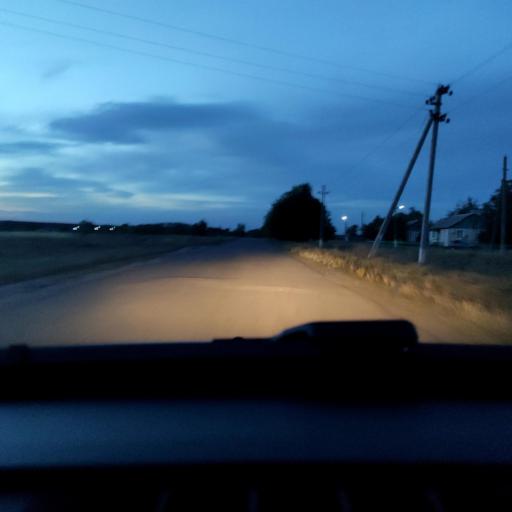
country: RU
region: Voronezj
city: Sadovoye
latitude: 51.6216
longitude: 40.4884
